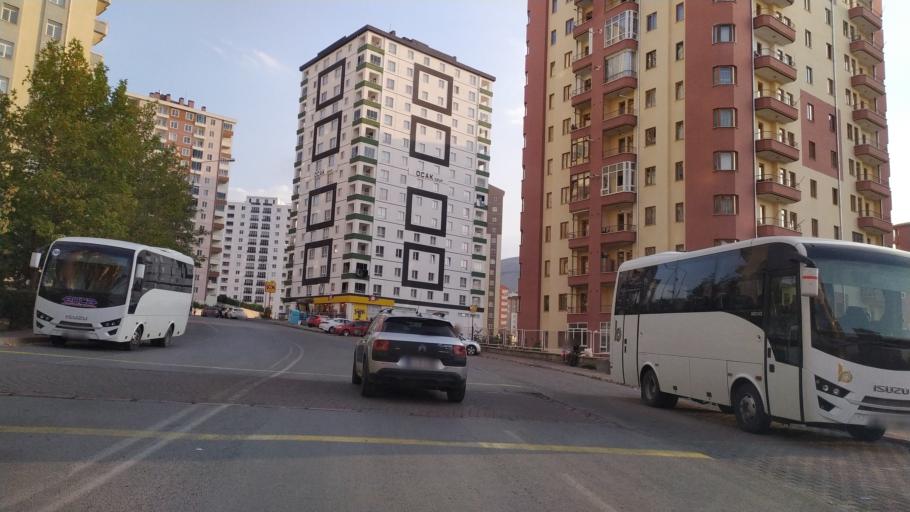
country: TR
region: Kayseri
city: Talas
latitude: 38.7041
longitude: 35.5615
